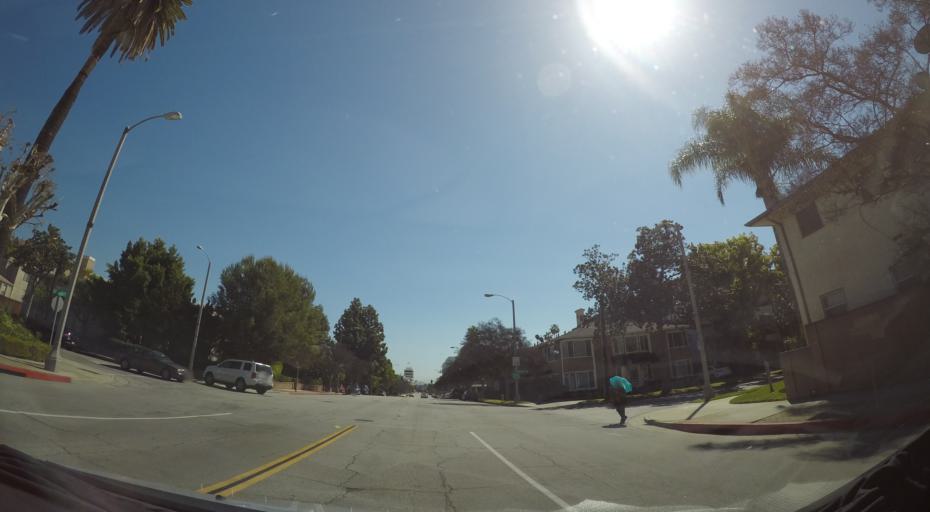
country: US
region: California
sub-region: Los Angeles County
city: Pasadena
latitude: 34.1426
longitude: -118.1386
